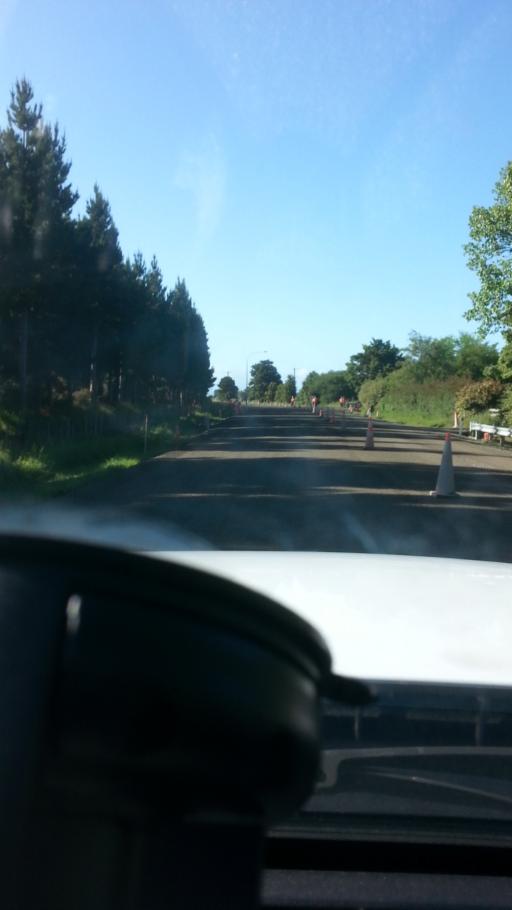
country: NZ
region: Wellington
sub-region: Masterton District
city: Masterton
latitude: -40.8078
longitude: 175.6201
